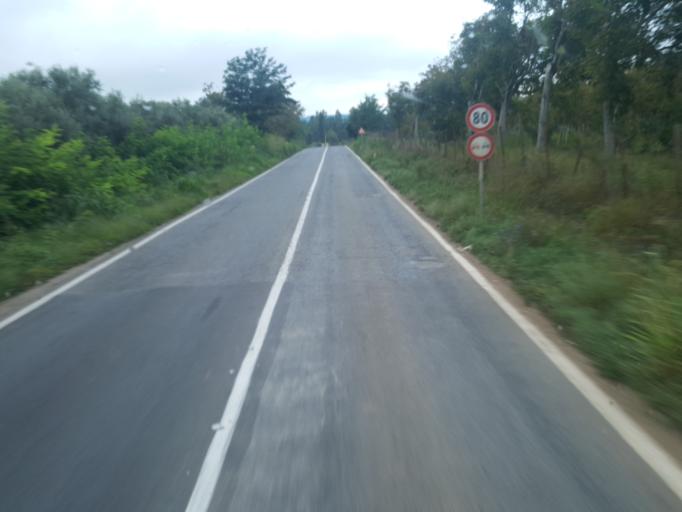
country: IT
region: Campania
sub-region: Provincia di Caserta
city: Sparanise
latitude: 41.1743
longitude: 14.1287
